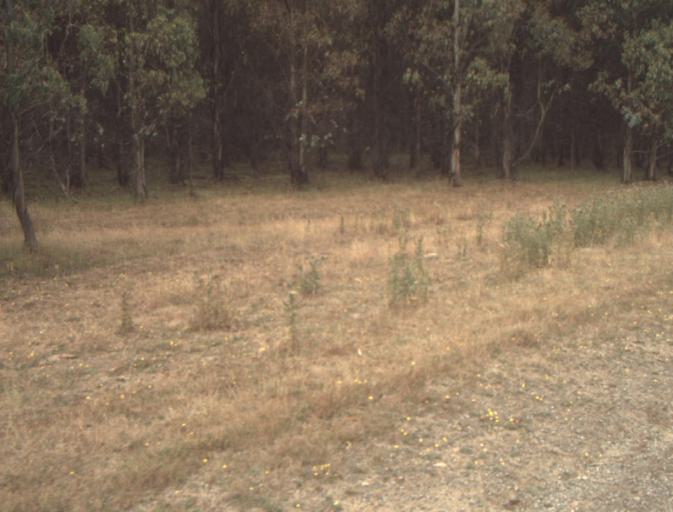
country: AU
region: Tasmania
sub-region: Dorset
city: Scottsdale
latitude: -41.4691
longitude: 147.5975
